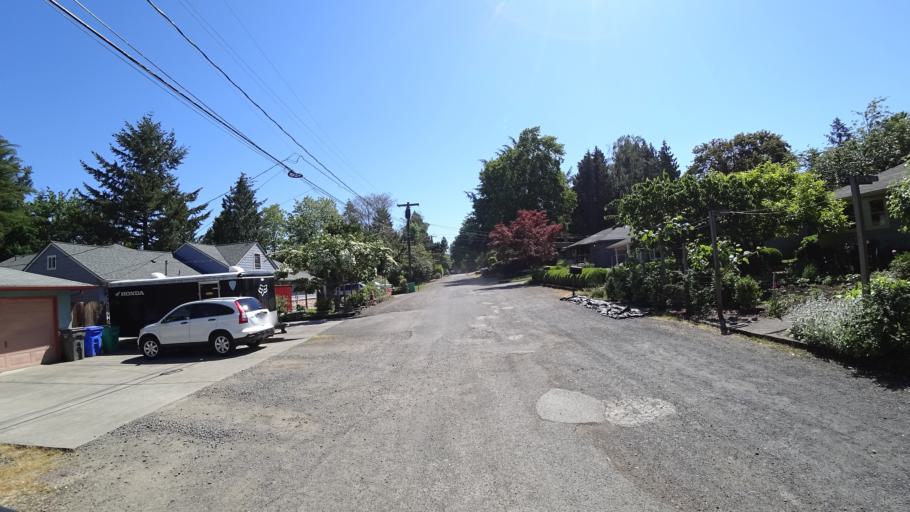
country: US
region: Oregon
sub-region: Washington County
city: Raleigh Hills
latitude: 45.4850
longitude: -122.7307
